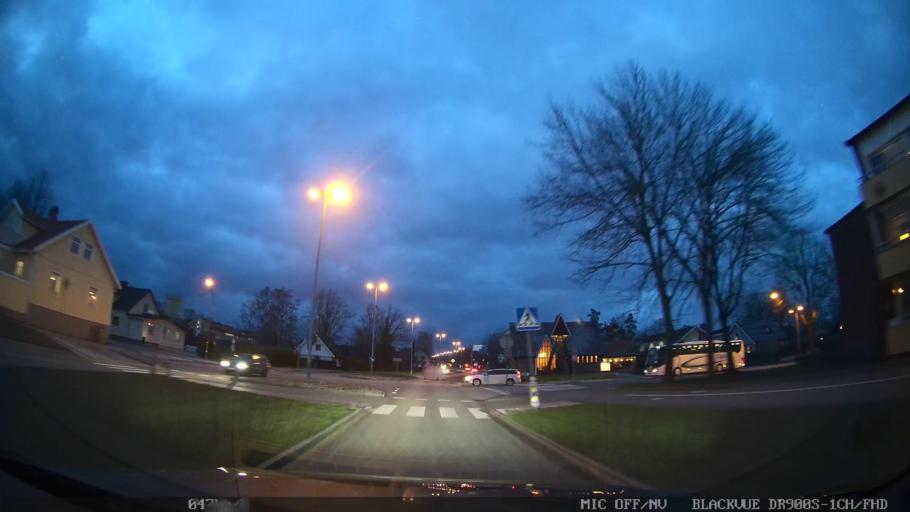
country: SE
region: Skane
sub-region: Hassleholms Kommun
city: Hassleholm
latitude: 56.1607
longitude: 13.7561
